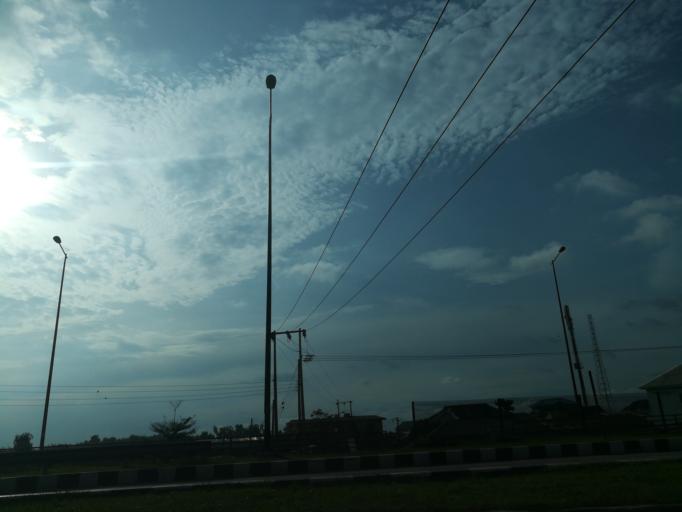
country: NG
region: Lagos
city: Ebute Ikorodu
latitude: 6.6114
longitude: 3.4411
